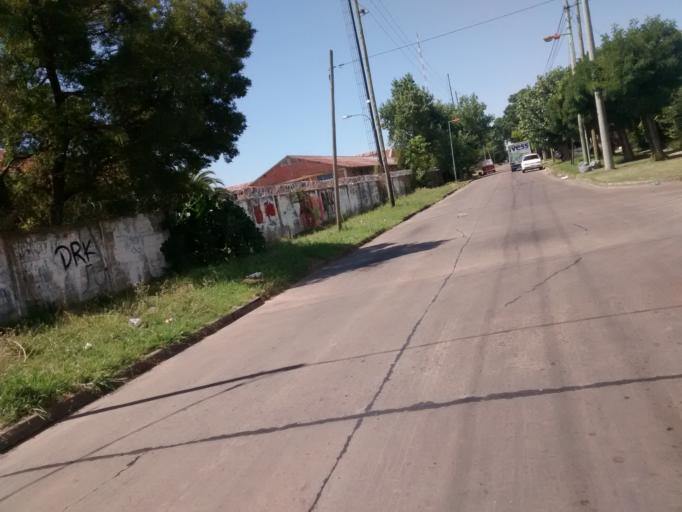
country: AR
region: Buenos Aires
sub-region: Partido de La Plata
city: La Plata
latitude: -34.9480
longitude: -57.9796
